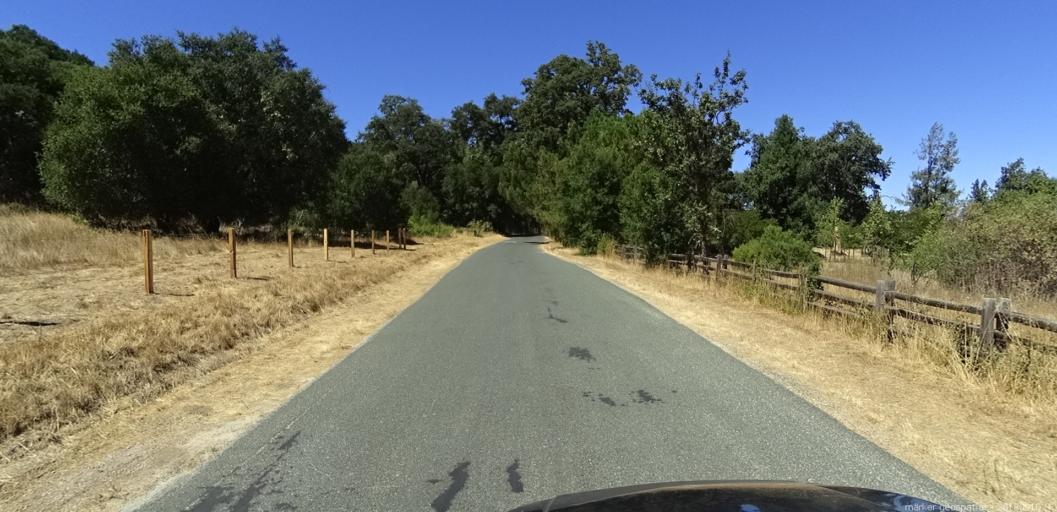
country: US
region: California
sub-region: Monterey County
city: Carmel Valley Village
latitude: 36.4388
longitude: -121.7952
